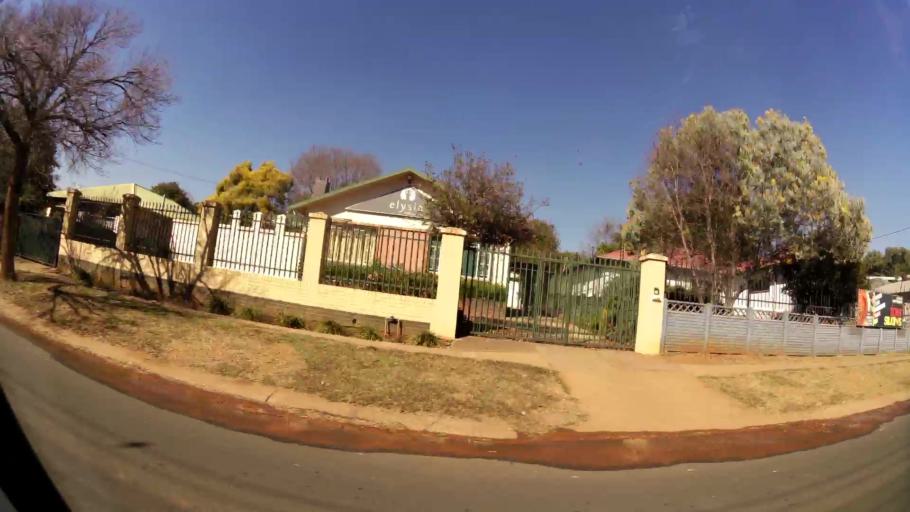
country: ZA
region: Gauteng
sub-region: City of Tshwane Metropolitan Municipality
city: Pretoria
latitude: -25.7739
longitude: 28.2286
